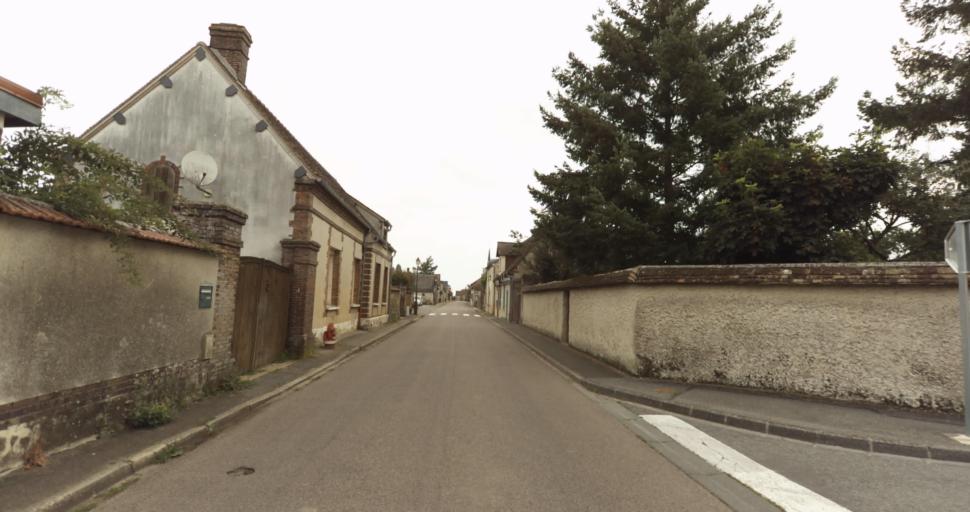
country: FR
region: Haute-Normandie
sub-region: Departement de l'Eure
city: Marcilly-sur-Eure
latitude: 48.8645
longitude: 1.3425
